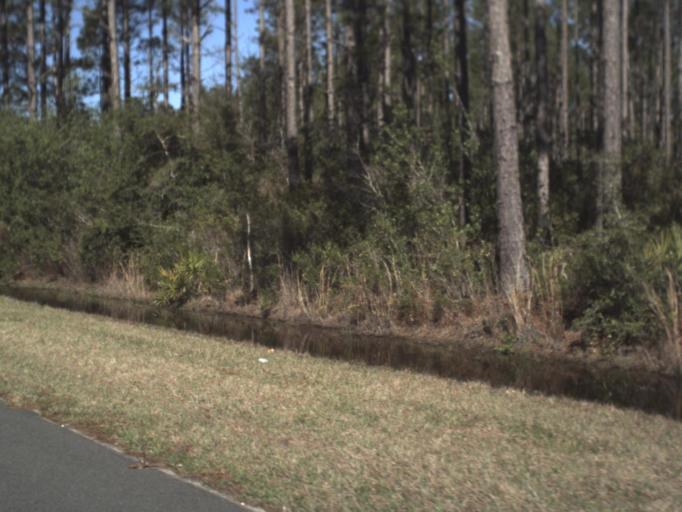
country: US
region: Florida
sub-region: Bay County
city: Callaway
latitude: 30.1457
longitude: -85.4409
